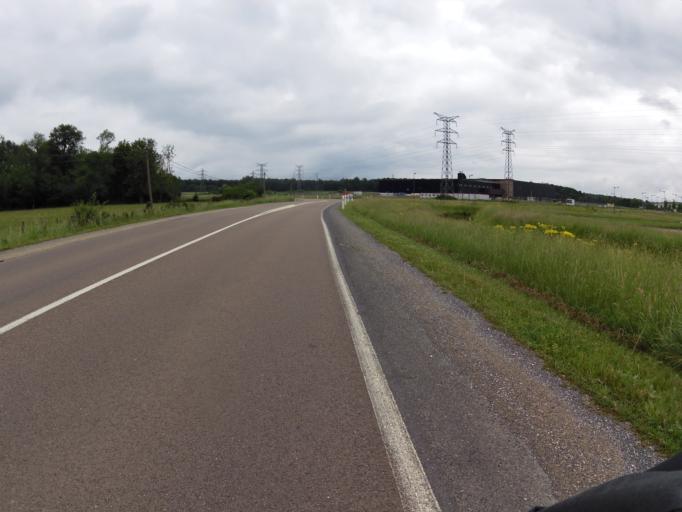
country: FR
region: Champagne-Ardenne
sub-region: Departement de la Haute-Marne
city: Saint-Dizier
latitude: 48.6547
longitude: 4.9378
